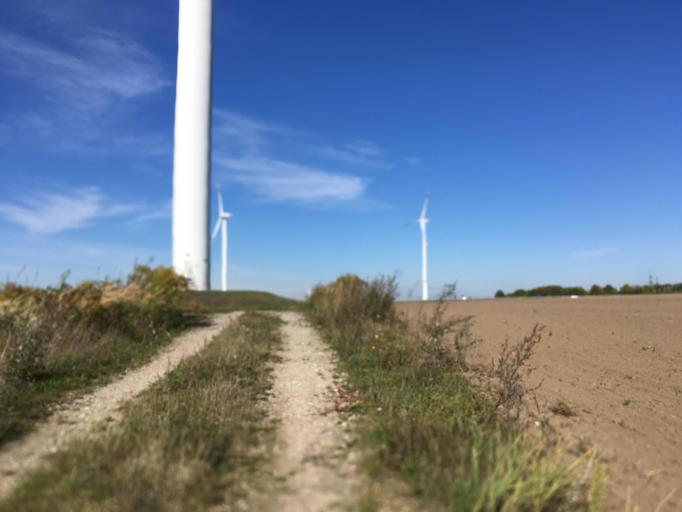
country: DE
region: Berlin
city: Falkenberg
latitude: 52.6094
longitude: 13.5400
